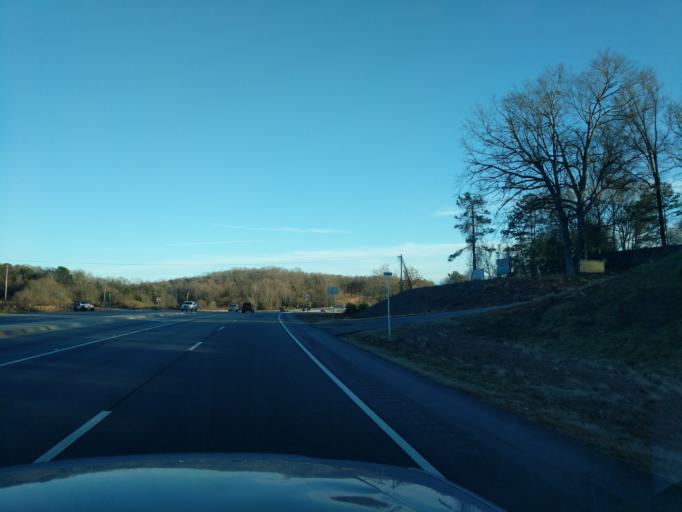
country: US
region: Georgia
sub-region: Stephens County
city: Toccoa
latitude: 34.5336
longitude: -83.2564
